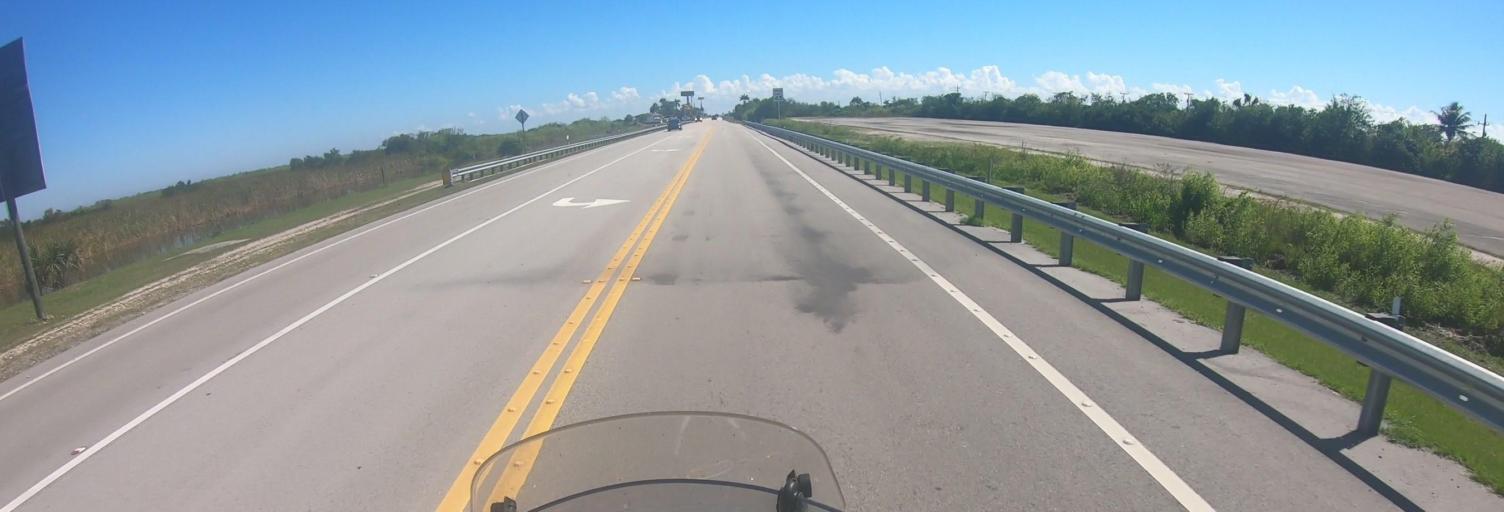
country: US
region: Florida
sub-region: Miami-Dade County
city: Kendall West
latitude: 25.7616
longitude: -80.7739
